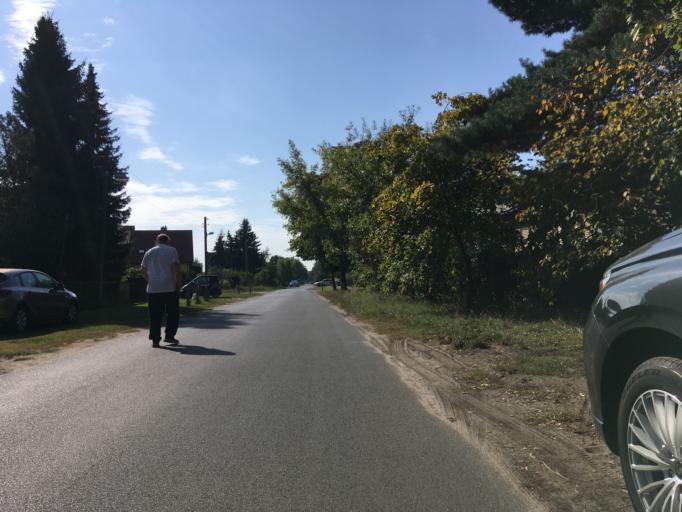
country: DE
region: Berlin
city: Mahlsdorf
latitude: 52.4903
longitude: 13.6029
